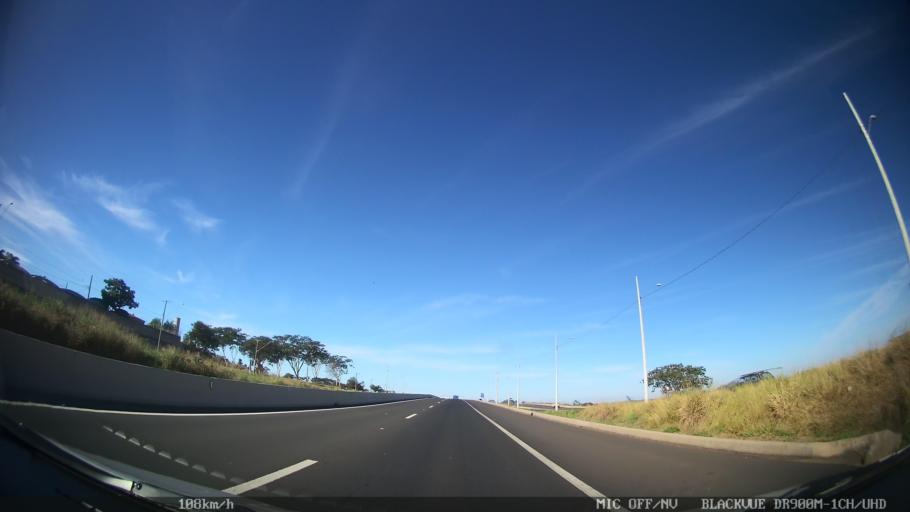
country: BR
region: Sao Paulo
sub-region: Sao Jose Do Rio Preto
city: Sao Jose do Rio Preto
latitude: -20.8516
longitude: -49.3909
